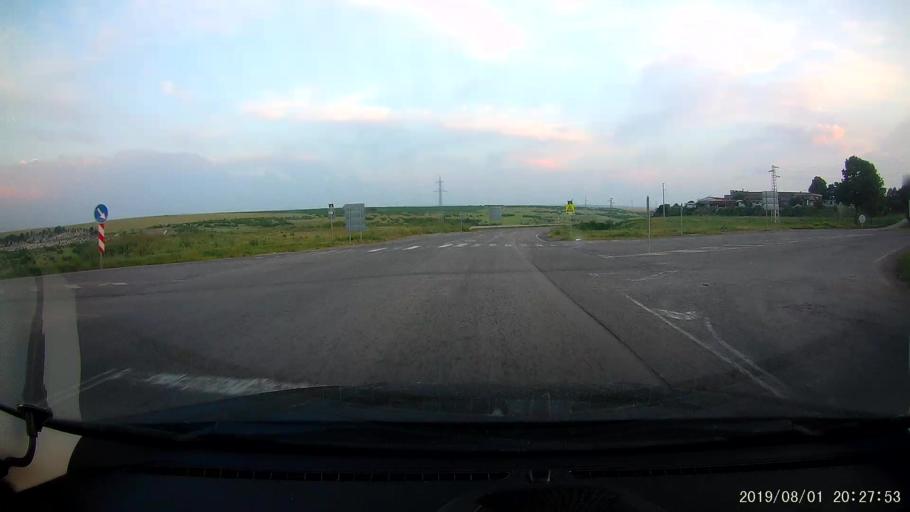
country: BG
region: Yambol
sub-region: Obshtina Elkhovo
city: Elkhovo
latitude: 42.1740
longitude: 26.5833
